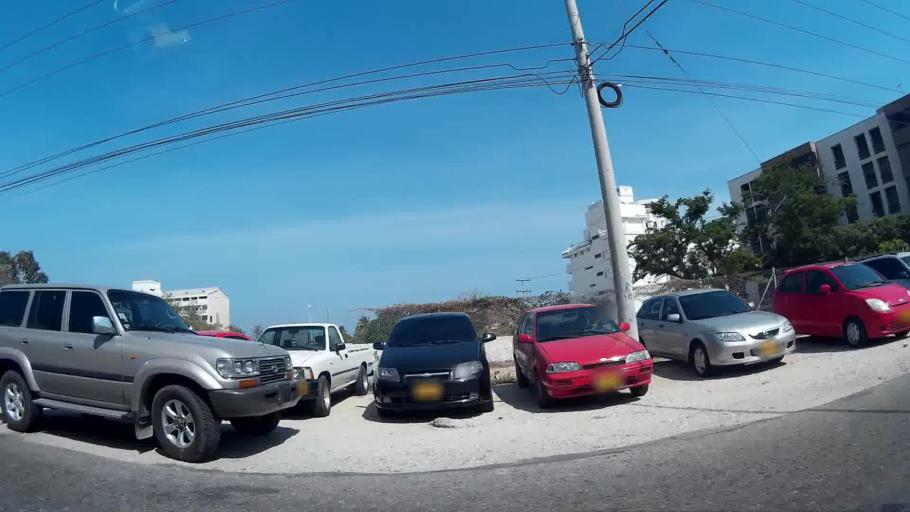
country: CO
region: Magdalena
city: Santa Marta
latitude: 11.2013
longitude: -74.2259
